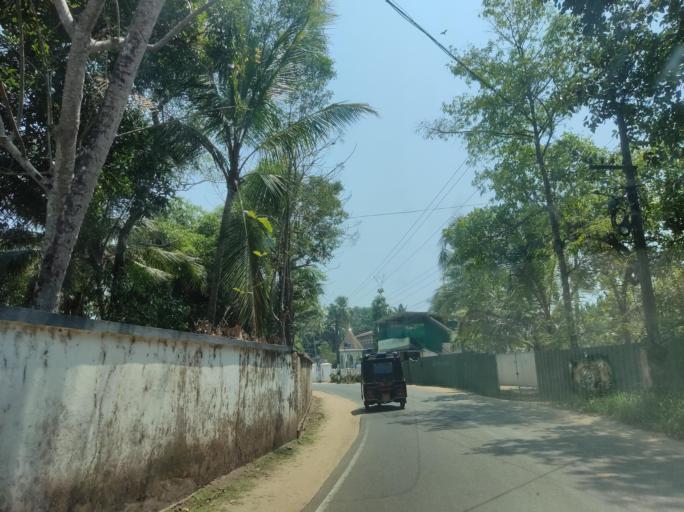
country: IN
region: Kerala
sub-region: Alappuzha
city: Kutiatodu
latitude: 9.8081
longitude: 76.3006
